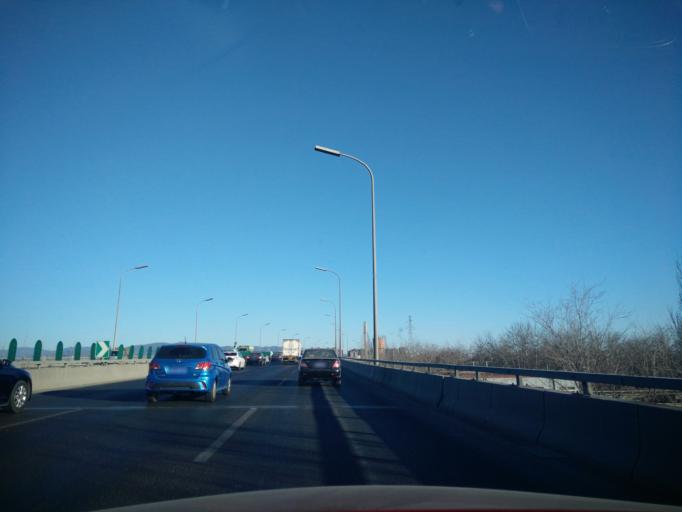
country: CN
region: Beijing
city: Lugu
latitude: 39.8745
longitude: 116.2021
